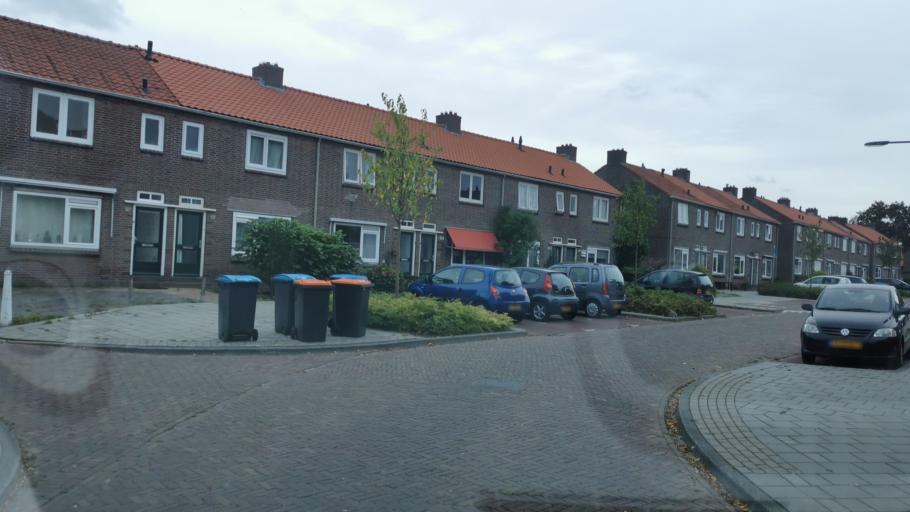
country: NL
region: Overijssel
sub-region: Gemeente Enschede
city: Enschede
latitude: 52.2283
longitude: 6.9111
